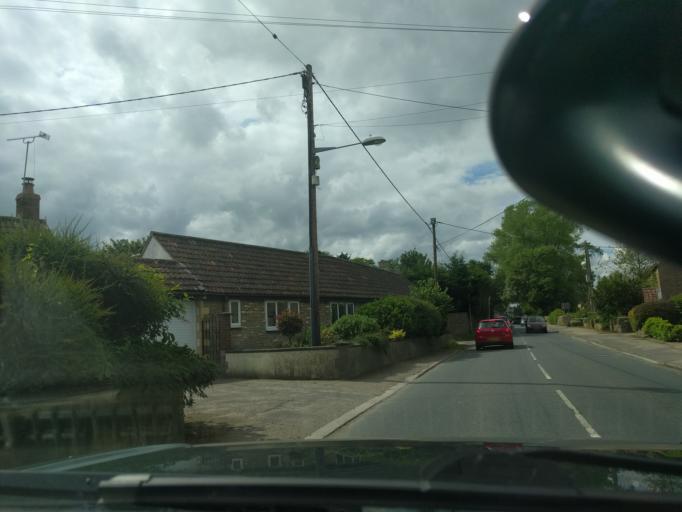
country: GB
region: England
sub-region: Wiltshire
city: Melksham
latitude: 51.3864
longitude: -2.1557
